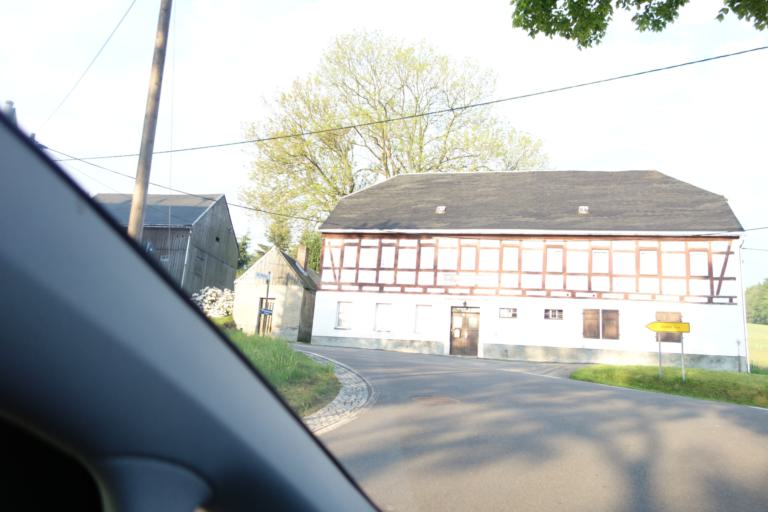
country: DE
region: Saxony
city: Pockau
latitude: 50.6804
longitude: 13.2498
